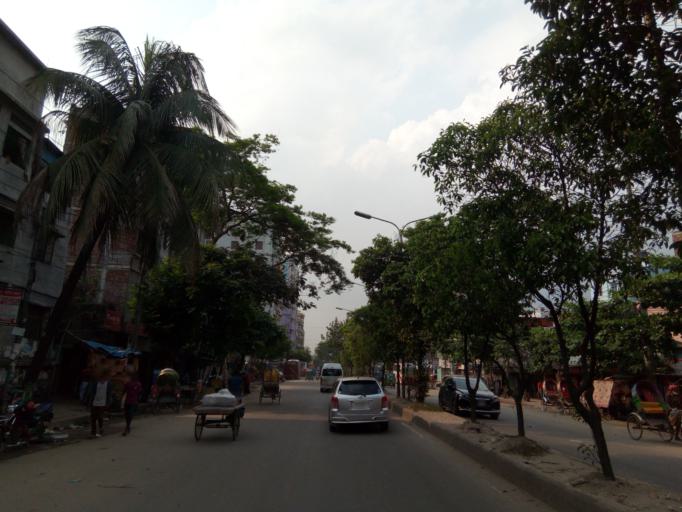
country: BD
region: Dhaka
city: Paltan
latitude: 23.7202
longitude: 90.4289
